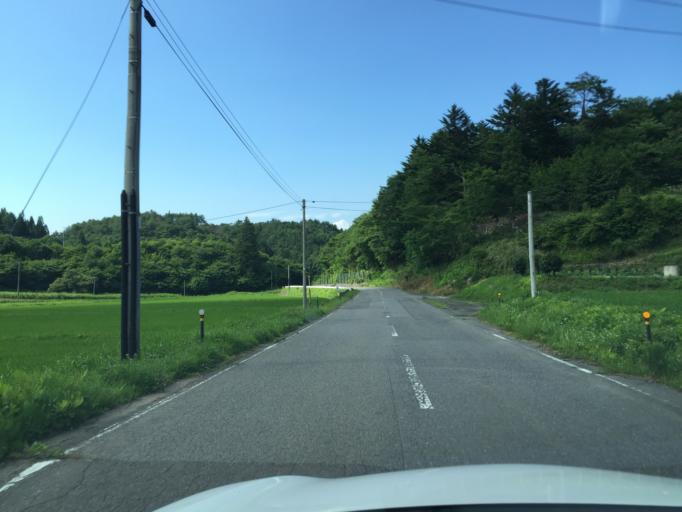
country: JP
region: Fukushima
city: Ishikawa
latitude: 37.1740
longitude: 140.6178
